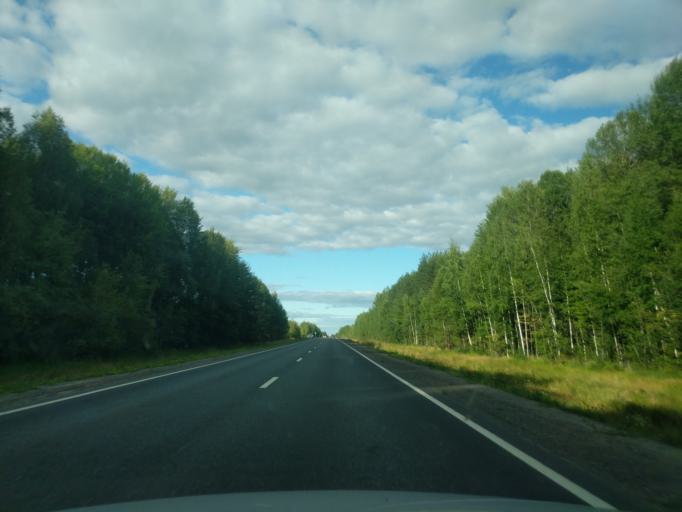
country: RU
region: Kostroma
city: Manturovo
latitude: 58.2256
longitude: 44.6252
